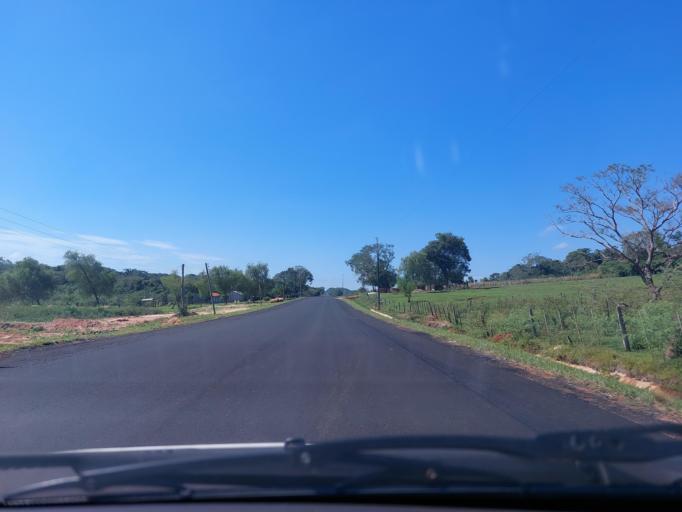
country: PY
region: San Pedro
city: Guayaybi
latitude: -24.5501
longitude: -56.5173
